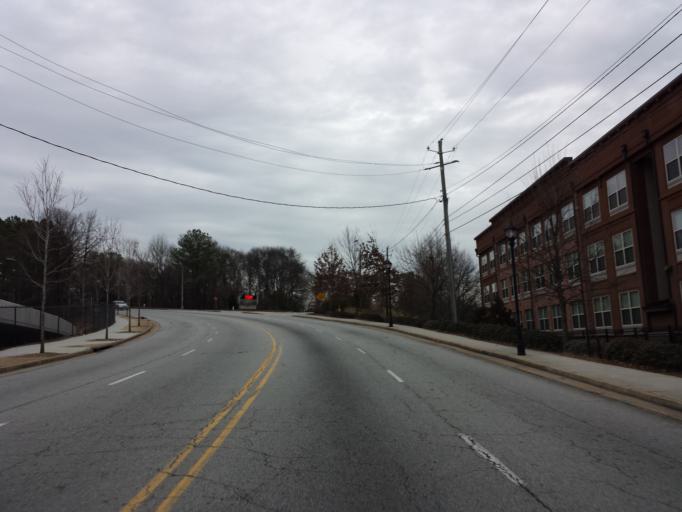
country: US
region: Georgia
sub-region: Fulton County
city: Atlanta
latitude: 33.7808
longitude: -84.4157
